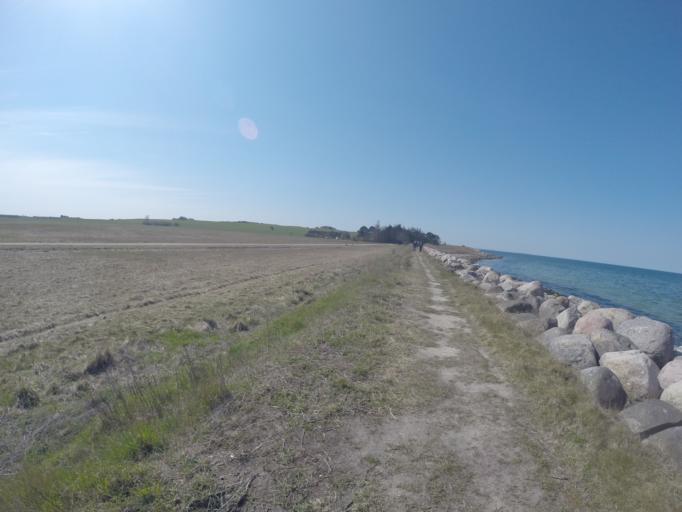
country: DK
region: Zealand
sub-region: Kalundborg Kommune
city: Gorlev
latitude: 55.5349
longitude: 11.0932
